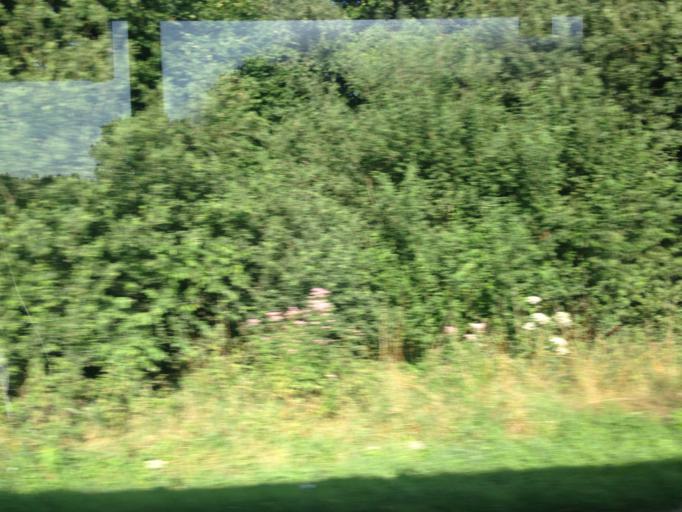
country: DE
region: North Rhine-Westphalia
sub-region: Regierungsbezirk Munster
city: Senden
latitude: 51.8735
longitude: 7.4929
